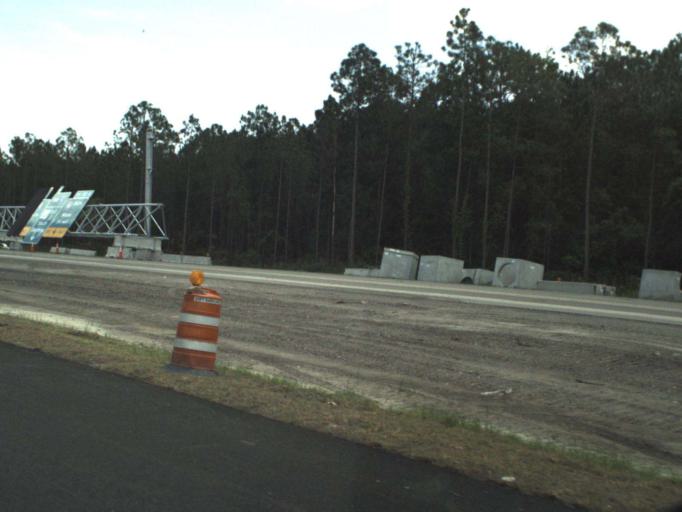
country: US
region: Florida
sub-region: Volusia County
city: South Daytona
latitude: 29.1463
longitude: -81.0974
